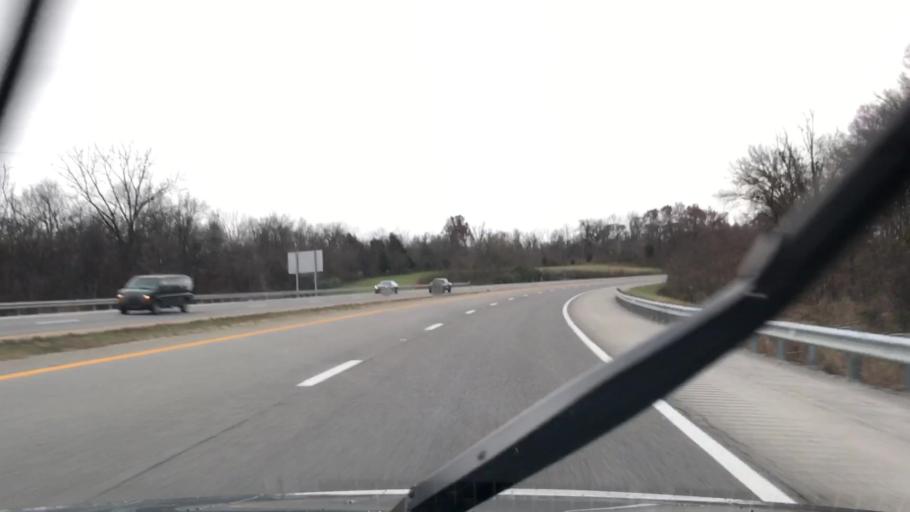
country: US
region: Kentucky
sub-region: Christian County
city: Hopkinsville
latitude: 36.8755
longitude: -87.4683
